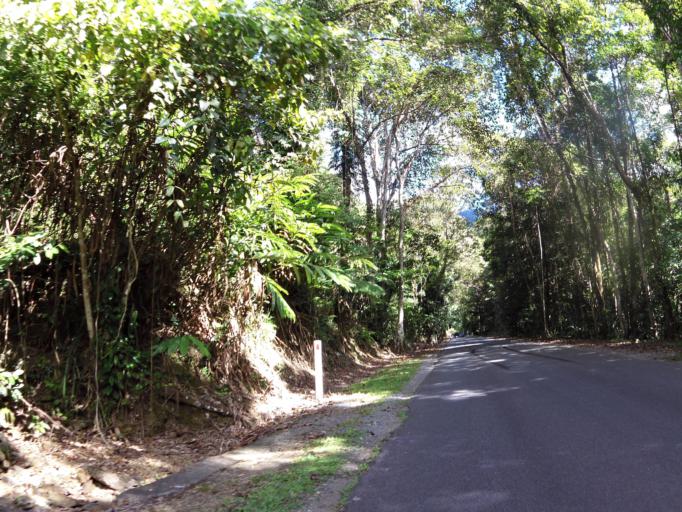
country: AU
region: Queensland
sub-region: Cairns
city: Woree
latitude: -16.9604
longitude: 145.6819
